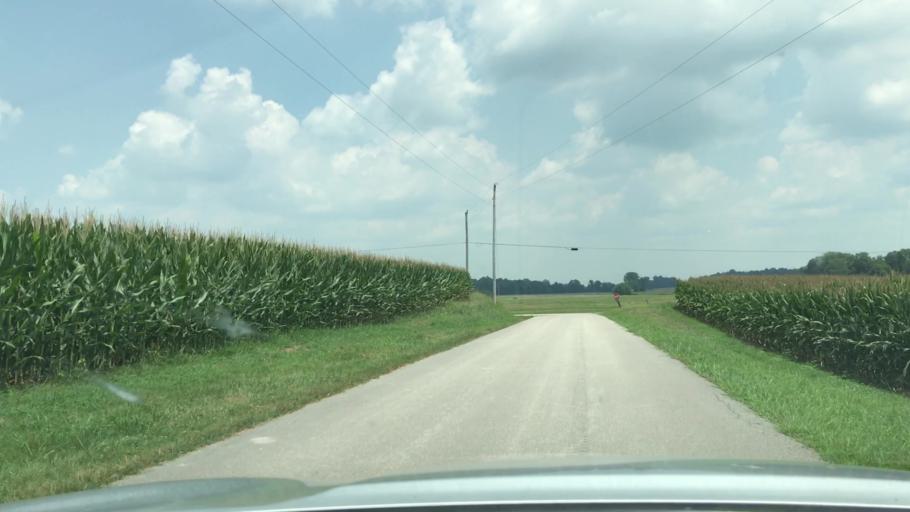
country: US
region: Kentucky
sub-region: Todd County
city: Elkton
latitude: 36.7670
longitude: -87.1128
